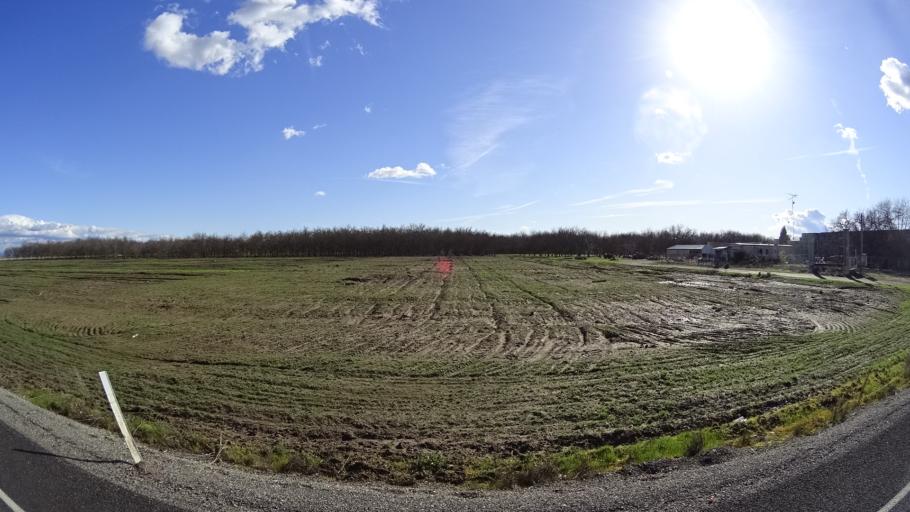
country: US
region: California
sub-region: Butte County
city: Gridley
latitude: 39.3642
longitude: -121.6326
